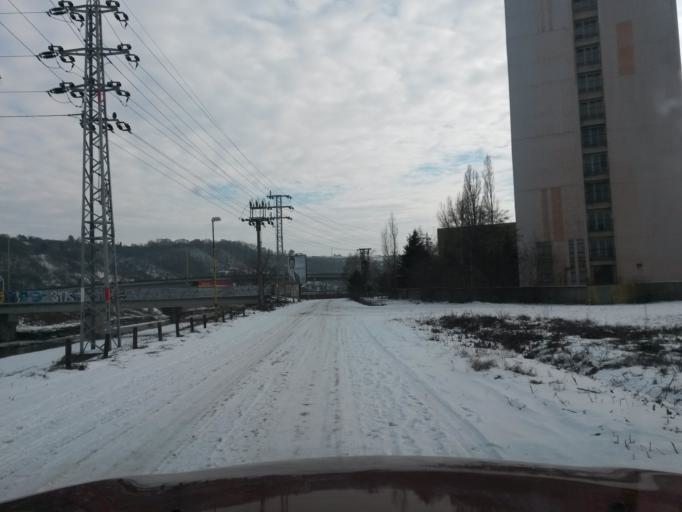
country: SK
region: Kosicky
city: Kosice
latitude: 48.7232
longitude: 21.2723
